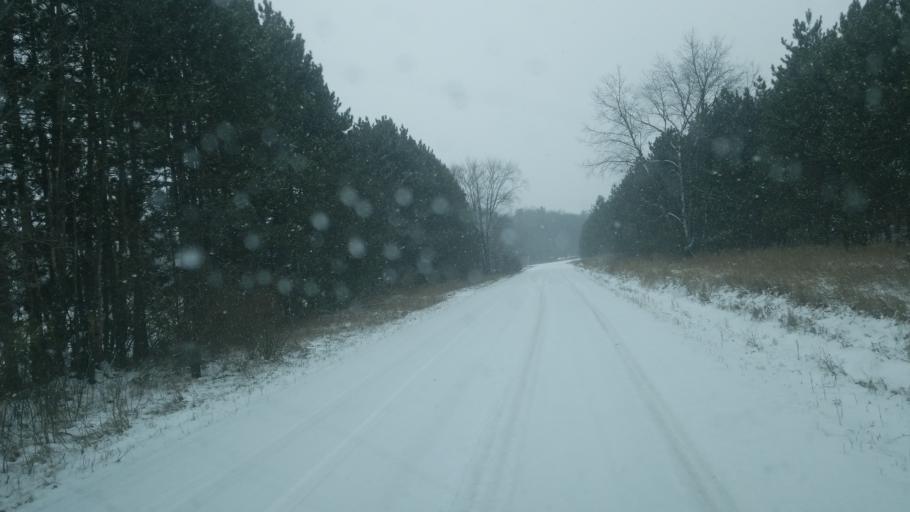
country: US
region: Michigan
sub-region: Osceola County
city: Reed City
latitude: 43.8413
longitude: -85.4141
